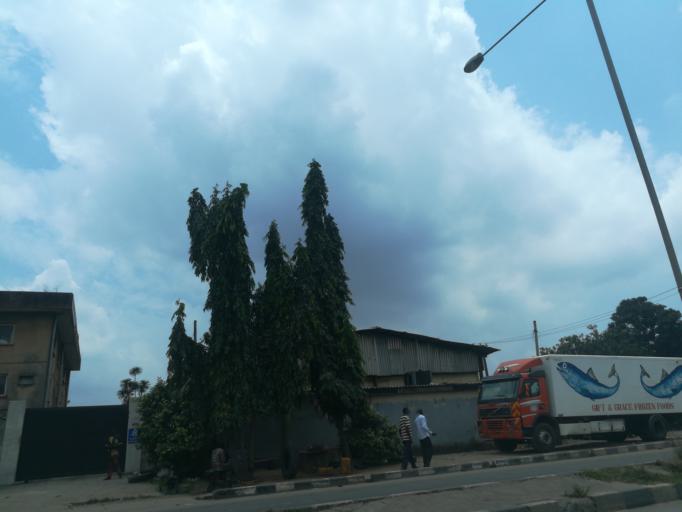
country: NG
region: Lagos
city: Ojota
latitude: 6.5921
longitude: 3.3728
